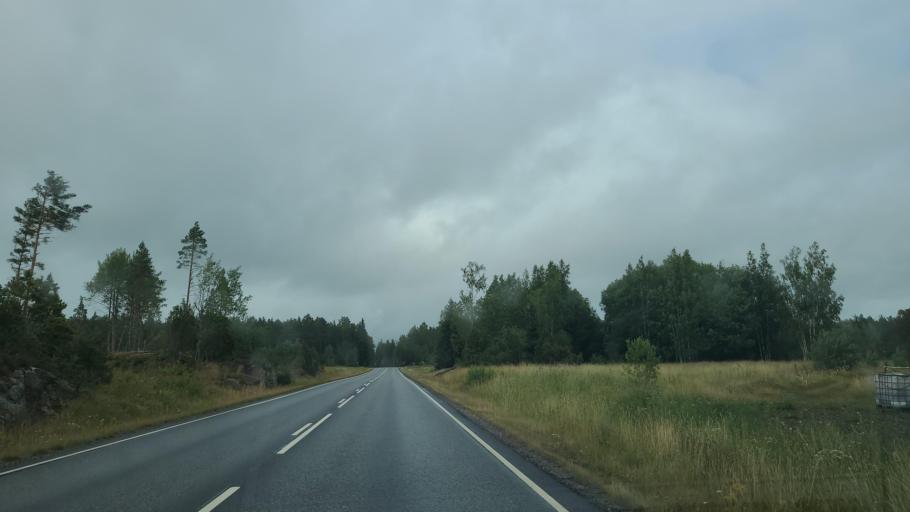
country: FI
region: Varsinais-Suomi
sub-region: Turku
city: Sauvo
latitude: 60.2412
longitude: 22.6118
